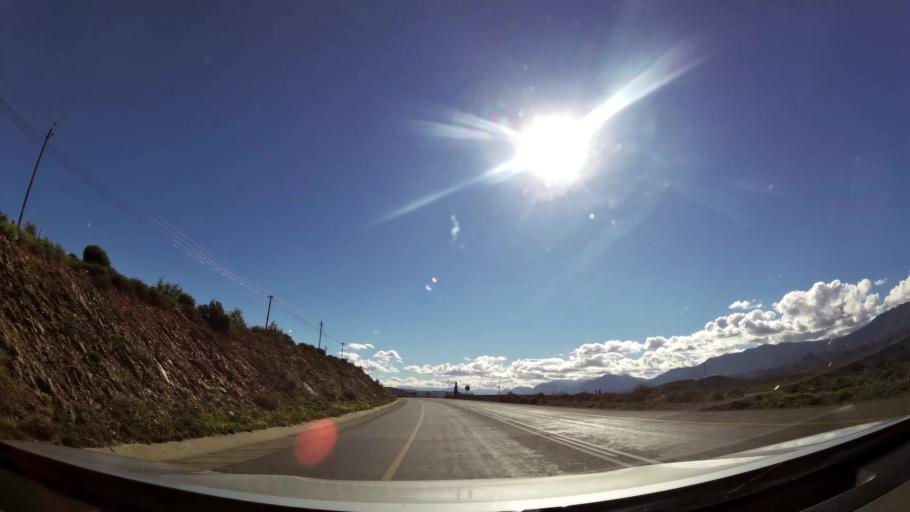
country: ZA
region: Western Cape
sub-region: Cape Winelands District Municipality
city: Ashton
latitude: -33.7786
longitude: 19.7643
